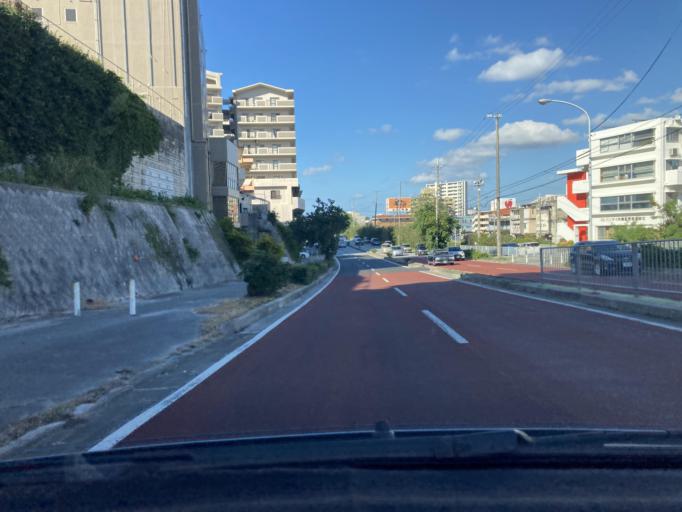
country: JP
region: Okinawa
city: Ginowan
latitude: 26.2624
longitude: 127.7262
